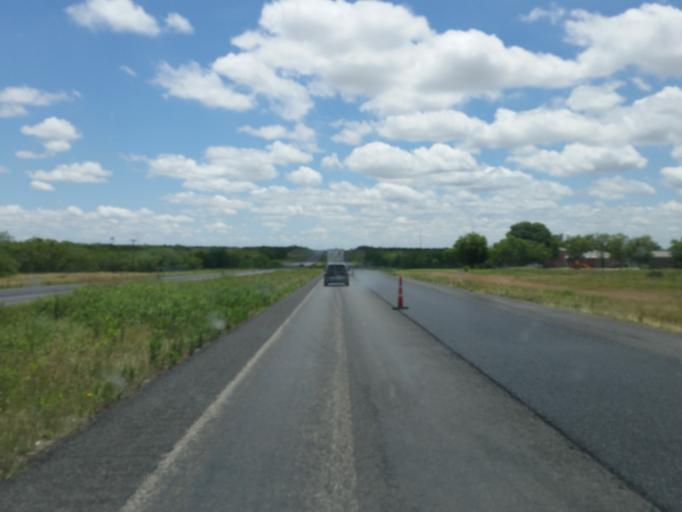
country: US
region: Texas
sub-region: Scurry County
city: Snyder
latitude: 32.7652
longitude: -100.9348
